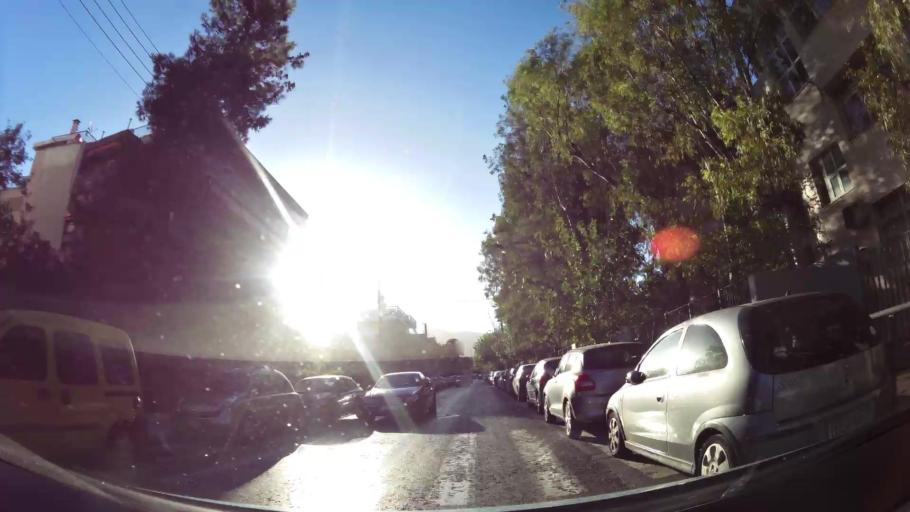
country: GR
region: Attica
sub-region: Nomarchia Athinas
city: Neo Psychiko
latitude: 38.0045
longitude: 23.7908
